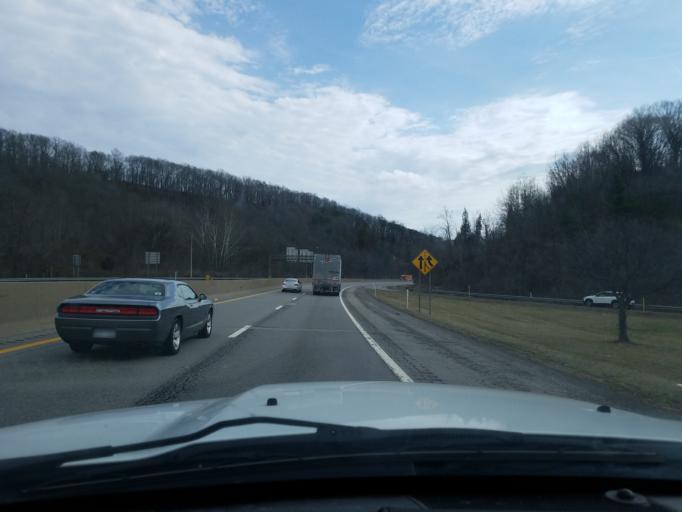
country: US
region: West Virginia
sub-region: Kanawha County
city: Nitro
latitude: 38.4400
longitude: -81.8311
